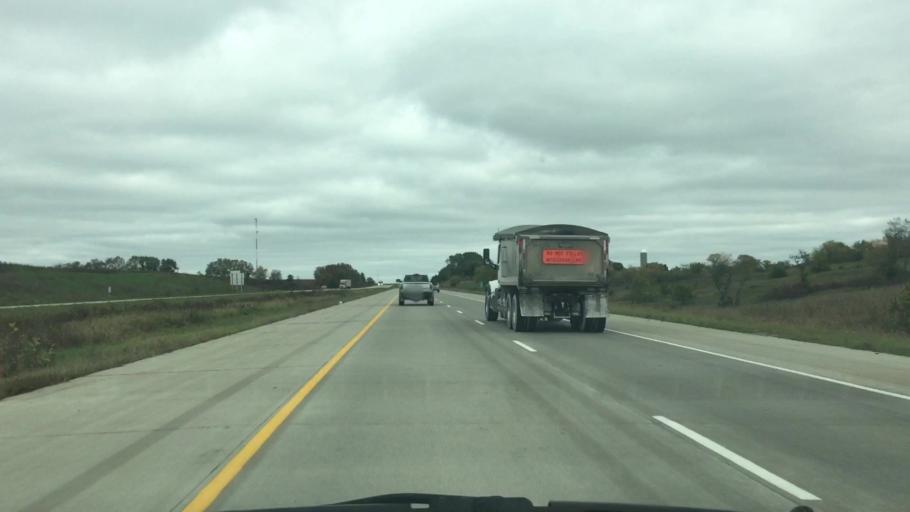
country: US
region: Iowa
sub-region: Warren County
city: Norwalk
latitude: 41.3794
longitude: -93.7805
